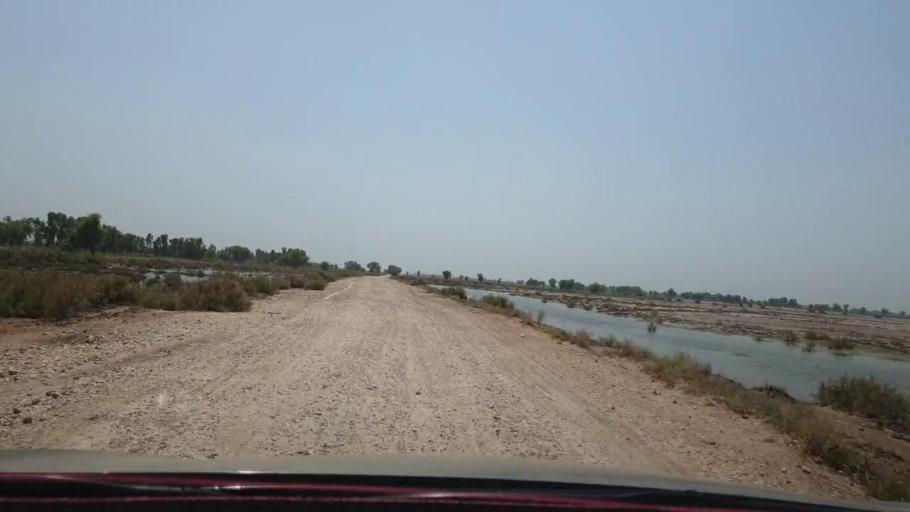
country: PK
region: Sindh
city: Kambar
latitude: 27.5733
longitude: 67.8797
